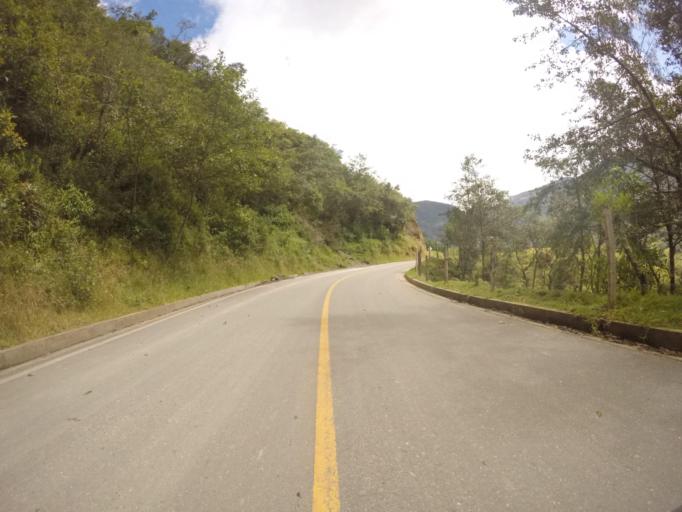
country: CO
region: Cauca
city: Jambalo
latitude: 2.7218
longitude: -76.3234
